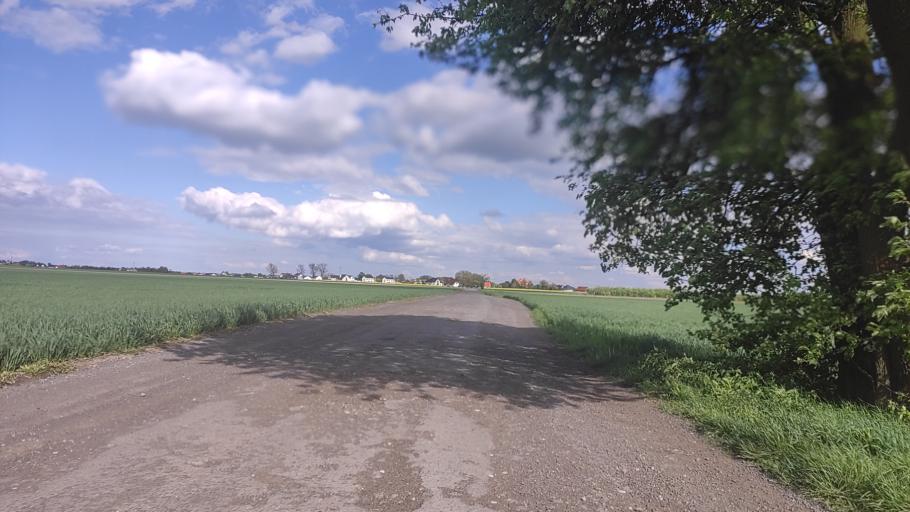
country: PL
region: Greater Poland Voivodeship
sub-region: Powiat poznanski
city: Swarzedz
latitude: 52.3873
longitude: 17.1337
